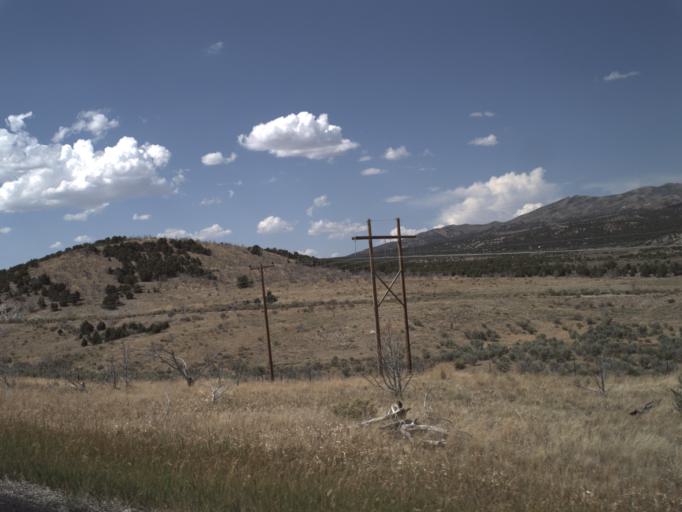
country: US
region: Idaho
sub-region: Minidoka County
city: Rupert
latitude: 41.9755
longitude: -113.1591
